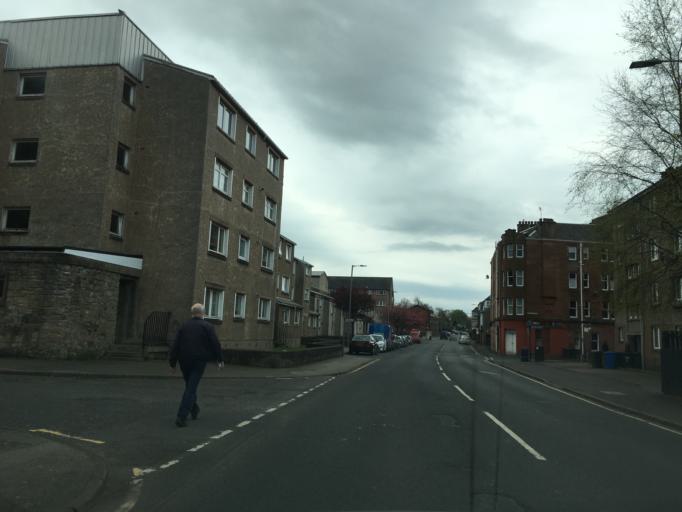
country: GB
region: Scotland
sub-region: Argyll and Bute
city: Rothesay
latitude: 55.8355
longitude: -5.0543
